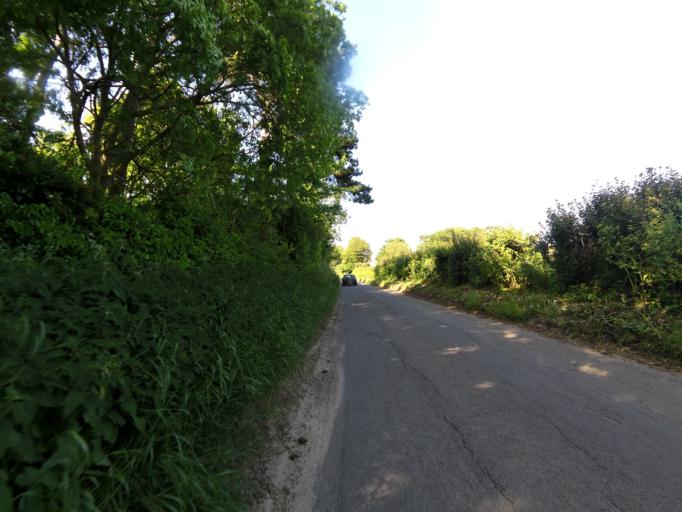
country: GB
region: England
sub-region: Suffolk
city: Felixstowe
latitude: 51.9992
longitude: 1.4139
